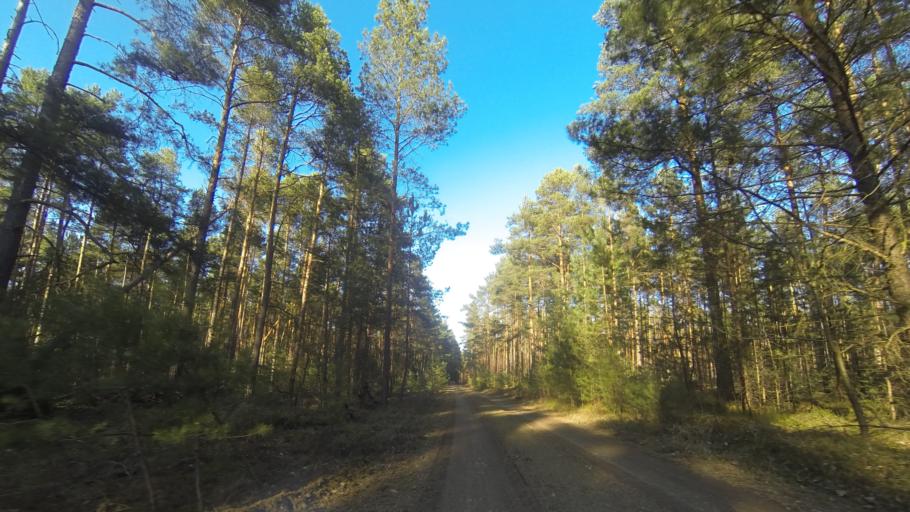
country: DE
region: Saxony
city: Laussnitz
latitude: 51.2594
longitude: 13.8505
